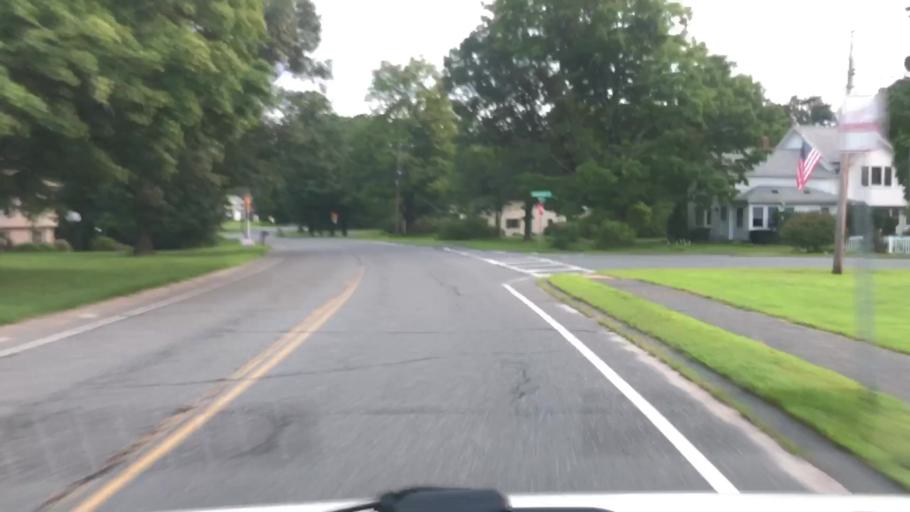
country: US
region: Massachusetts
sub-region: Hampshire County
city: Southampton
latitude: 42.2419
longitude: -72.7251
